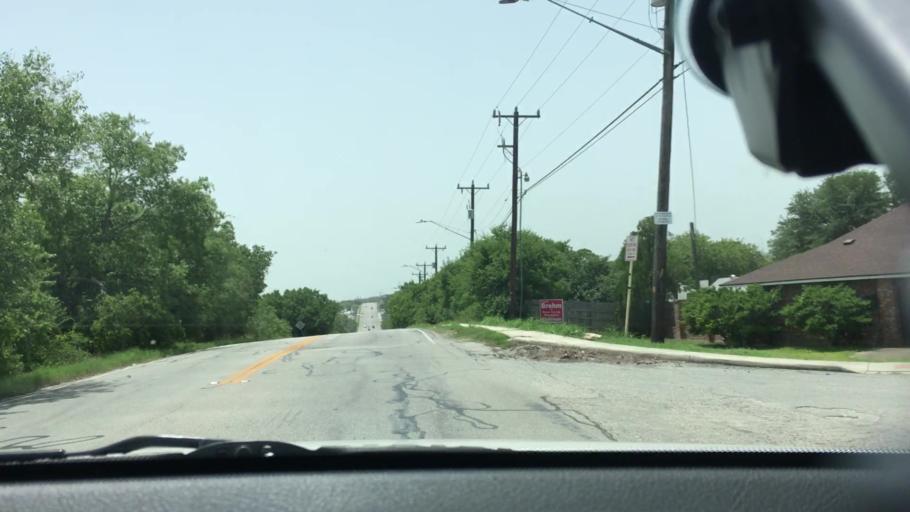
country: US
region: Texas
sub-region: Bexar County
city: Live Oak
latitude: 29.5747
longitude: -98.3597
